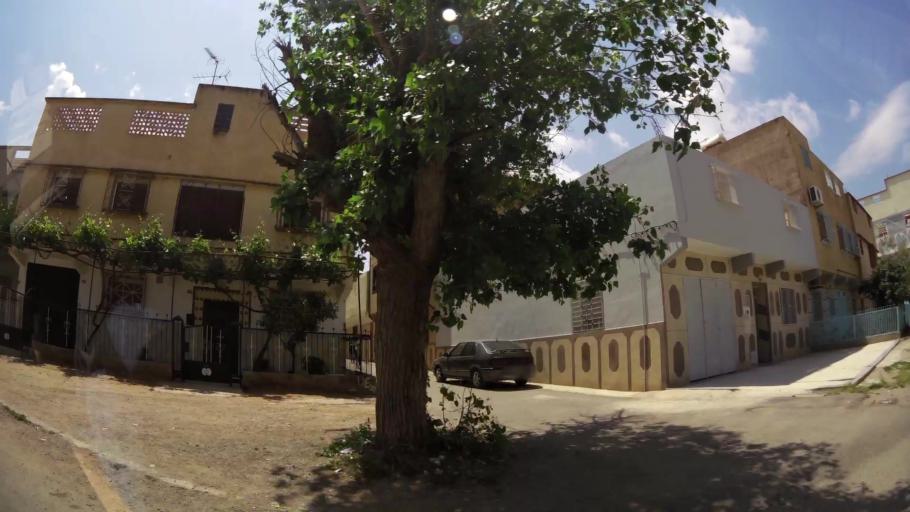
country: MA
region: Oriental
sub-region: Oujda-Angad
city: Oujda
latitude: 34.6836
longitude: -1.8865
